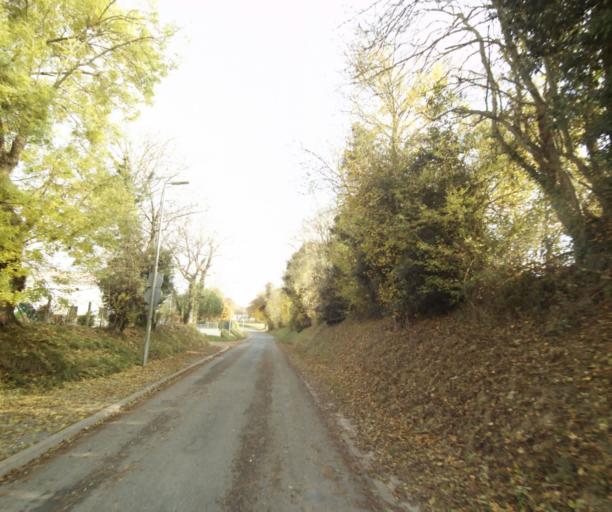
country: FR
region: Poitou-Charentes
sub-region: Departement de la Charente-Maritime
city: Saint-Georges-des-Coteaux
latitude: 45.7633
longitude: -0.7066
